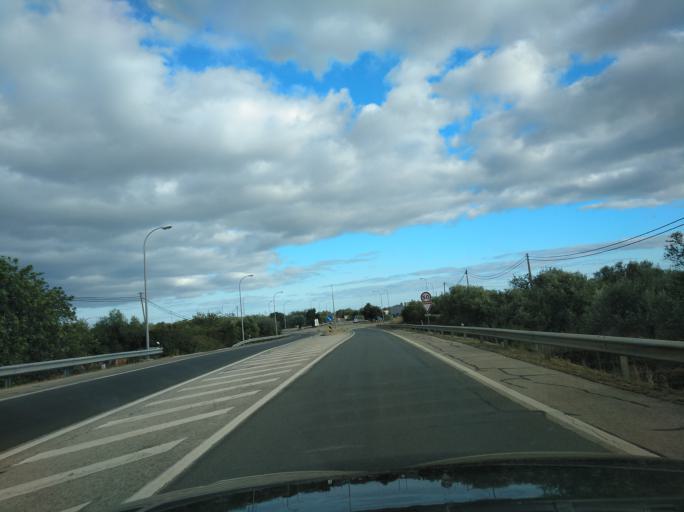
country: PT
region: Faro
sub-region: Tavira
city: Luz
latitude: 37.1355
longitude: -7.6964
